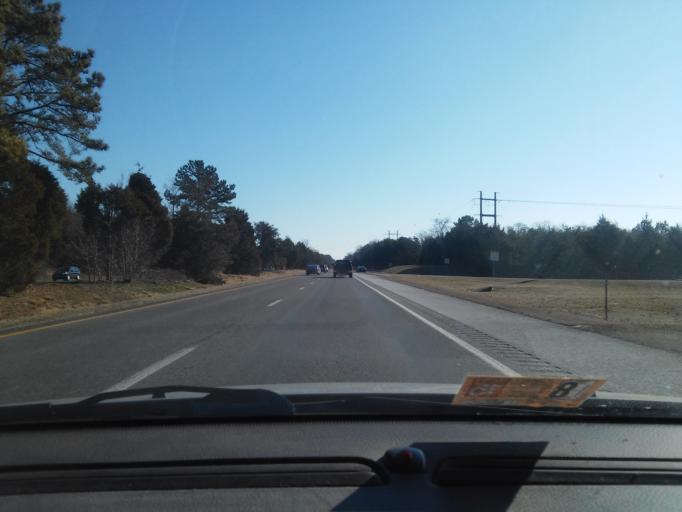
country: US
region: Virginia
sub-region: Henrico County
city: Wyndham
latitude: 37.7003
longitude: -77.7478
